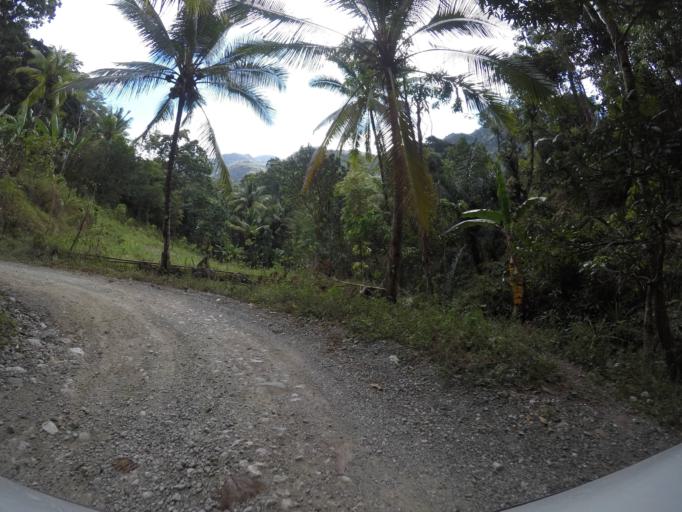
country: TL
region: Baucau
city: Baucau
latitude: -8.6209
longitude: 126.6566
